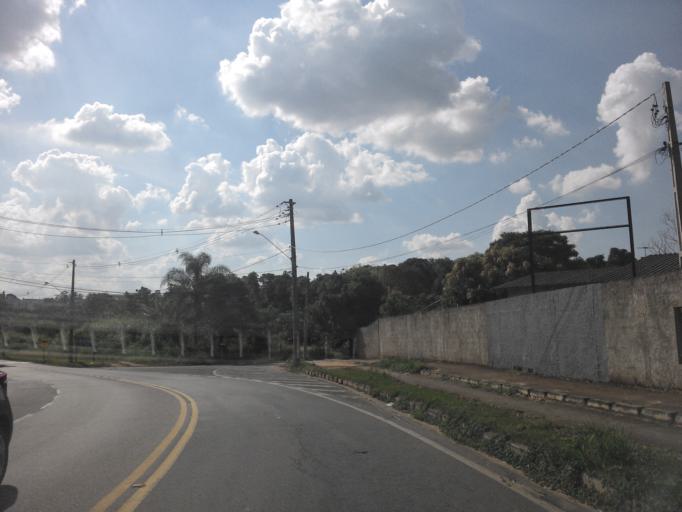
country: BR
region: Sao Paulo
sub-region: Valinhos
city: Valinhos
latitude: -22.9915
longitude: -47.0066
